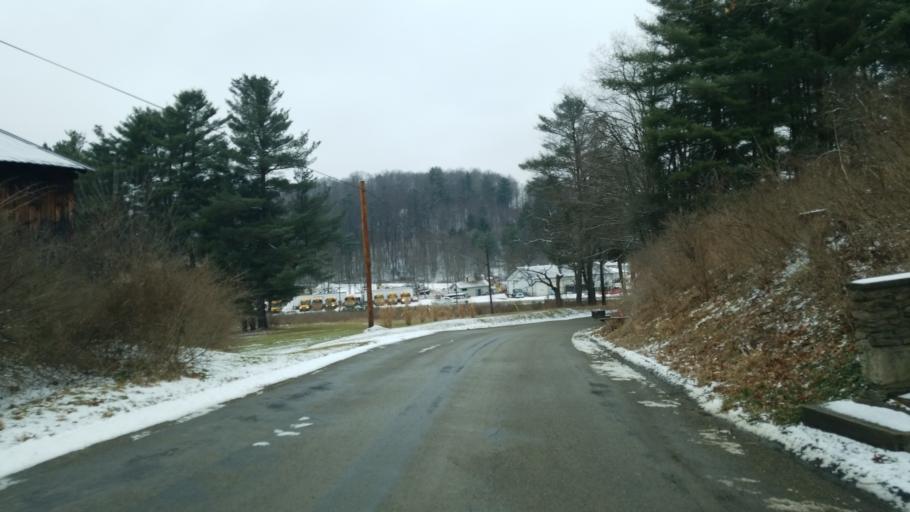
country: US
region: Pennsylvania
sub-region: Jefferson County
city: Reynoldsville
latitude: 41.0865
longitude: -78.8584
